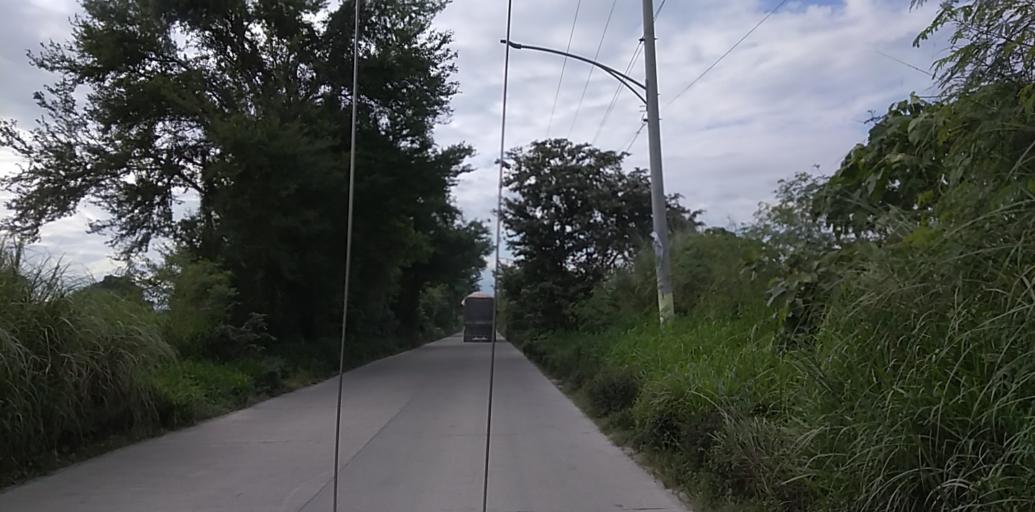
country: PH
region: Central Luzon
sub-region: Province of Pampanga
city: Porac
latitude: 15.0690
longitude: 120.5540
